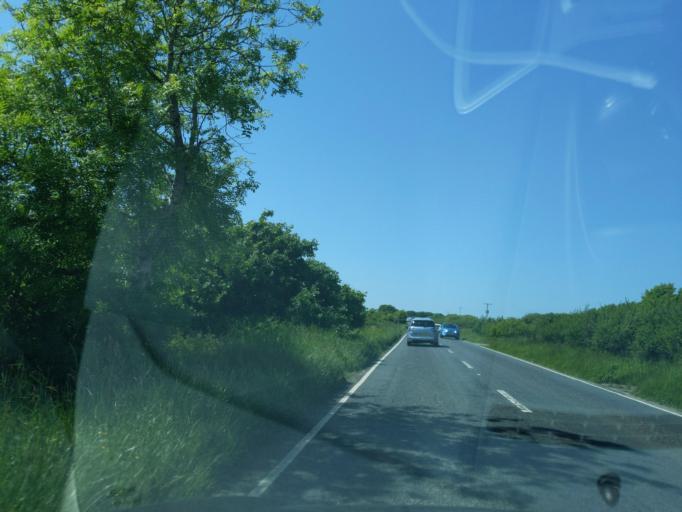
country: GB
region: England
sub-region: Cornwall
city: Trewen
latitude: 50.6466
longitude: -4.5317
